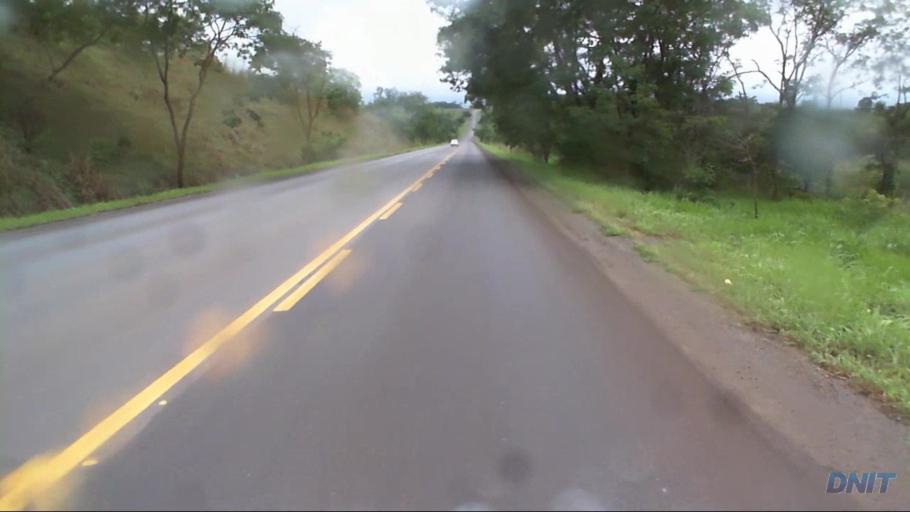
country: BR
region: Goias
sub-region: Padre Bernardo
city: Padre Bernardo
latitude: -15.1913
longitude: -48.4368
